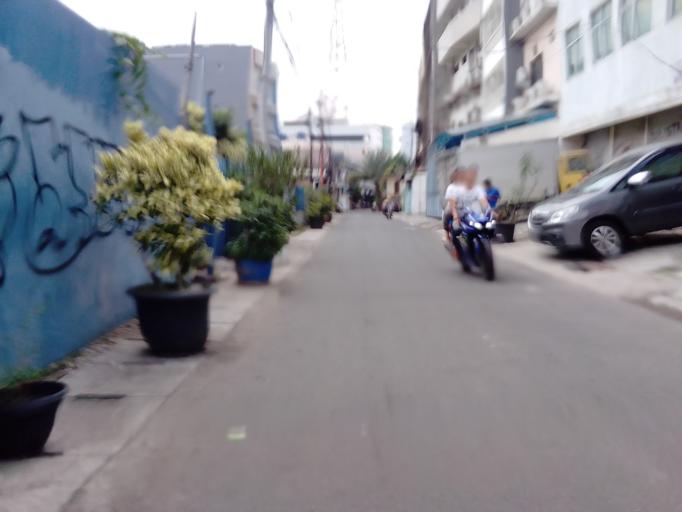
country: ID
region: Jakarta Raya
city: Jakarta
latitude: -6.1558
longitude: 106.8176
